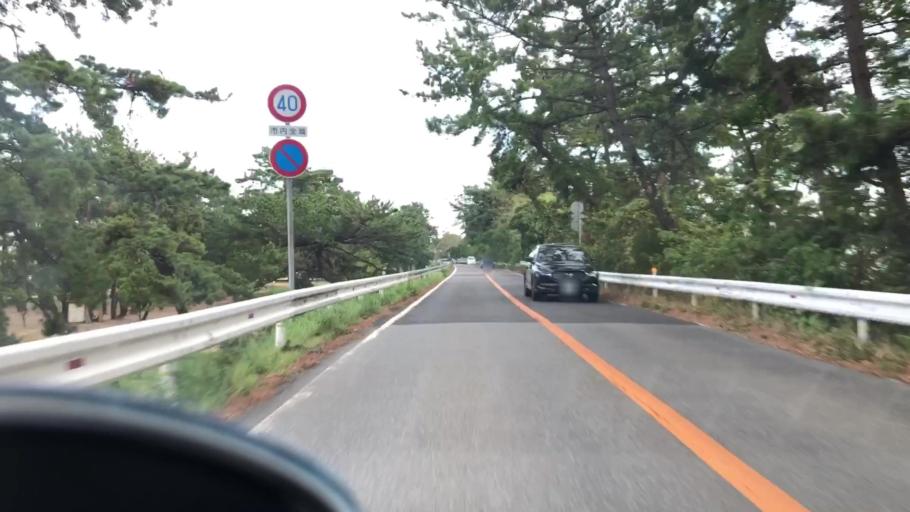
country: JP
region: Hyogo
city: Itami
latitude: 34.7572
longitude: 135.3720
